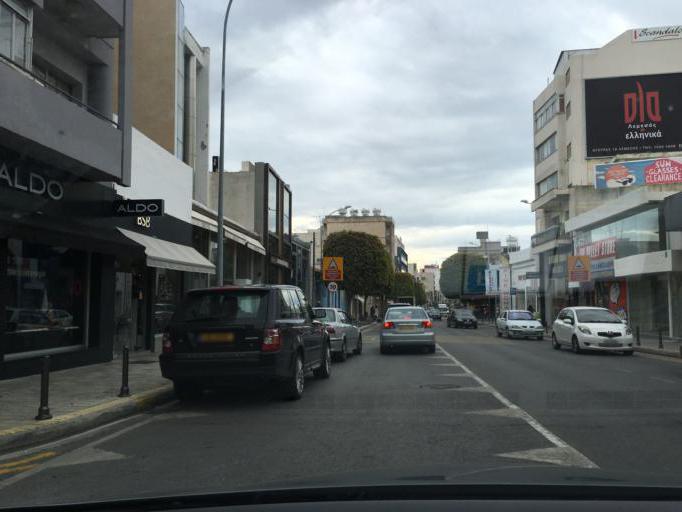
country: CY
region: Limassol
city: Limassol
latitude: 34.6803
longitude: 33.0435
